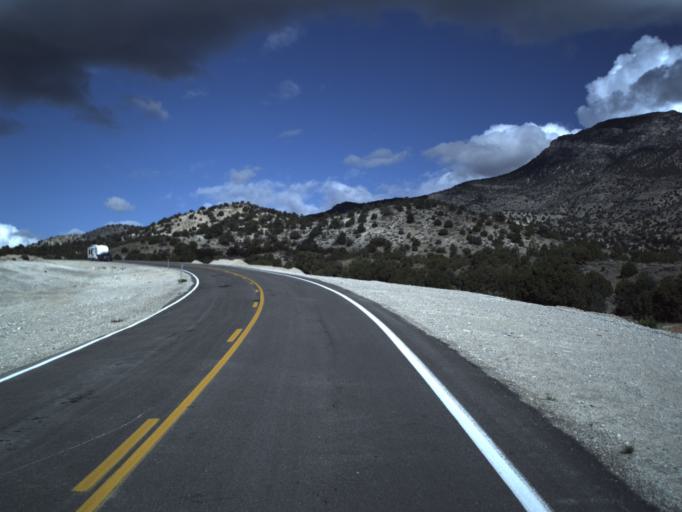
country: US
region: Utah
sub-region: Beaver County
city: Milford
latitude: 38.5117
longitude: -113.5250
